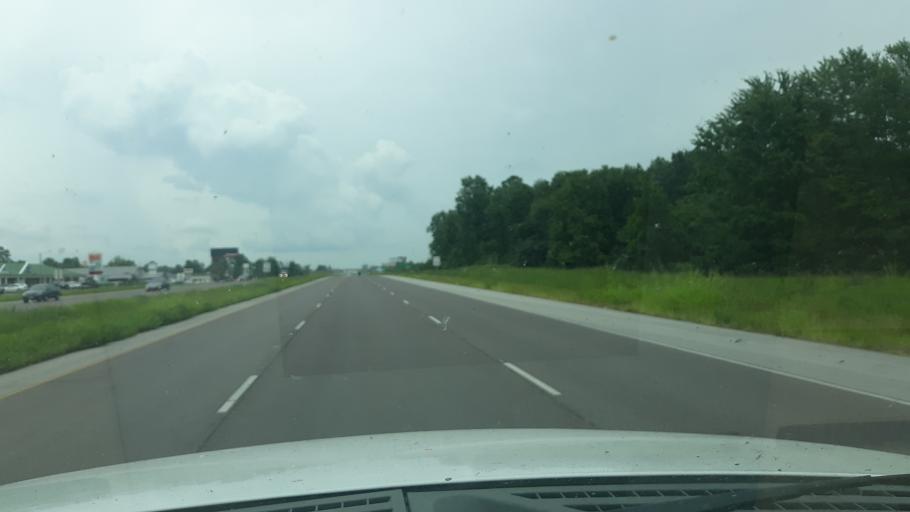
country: US
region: Illinois
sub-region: Williamson County
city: Crainville
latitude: 37.7450
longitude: -89.0742
